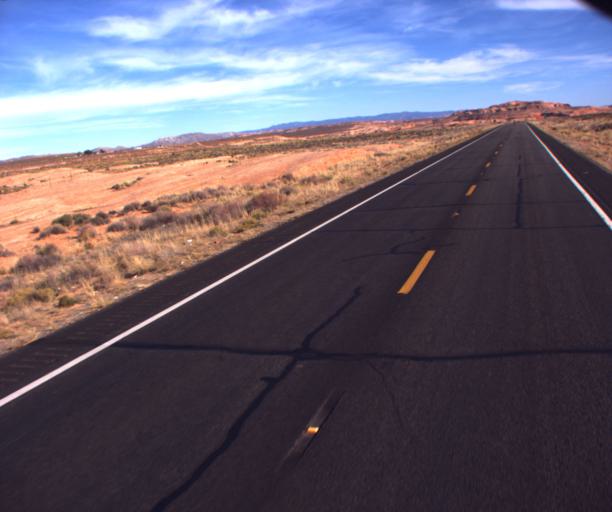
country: US
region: Arizona
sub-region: Apache County
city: Many Farms
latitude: 36.9306
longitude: -109.6245
